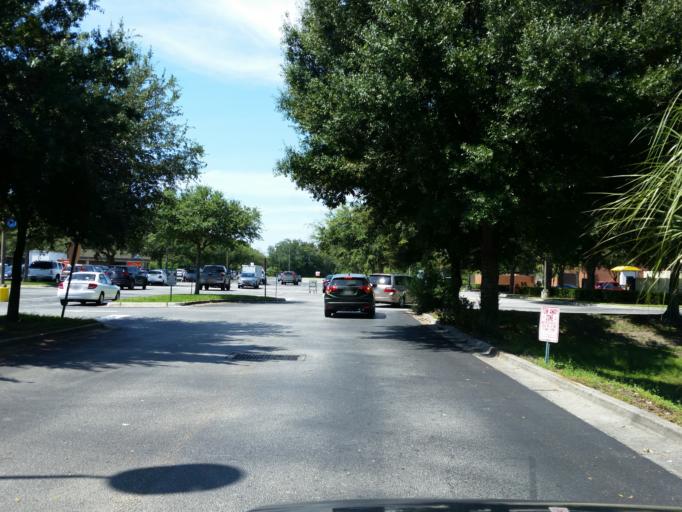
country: US
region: Florida
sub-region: Hillsborough County
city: Riverview
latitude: 27.8928
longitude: -82.3191
